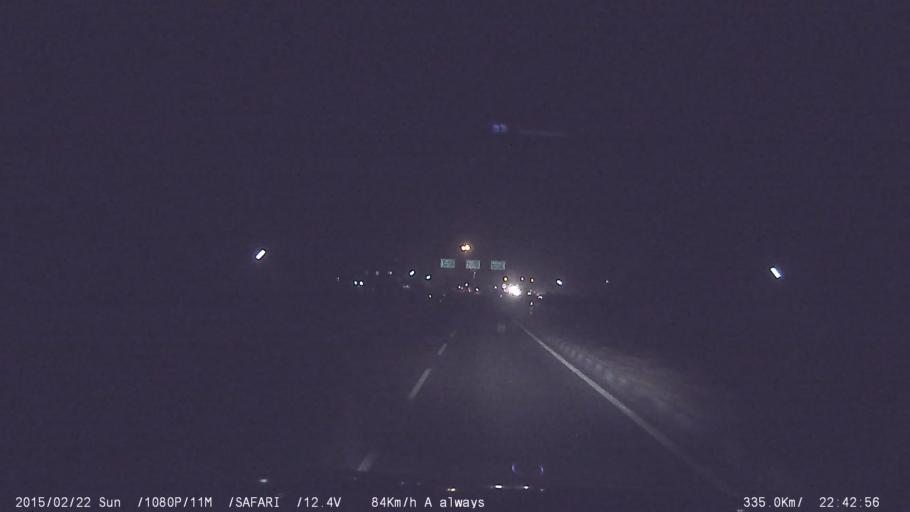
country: IN
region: Tamil Nadu
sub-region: Namakkal
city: Namakkal
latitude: 11.1907
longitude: 78.0879
